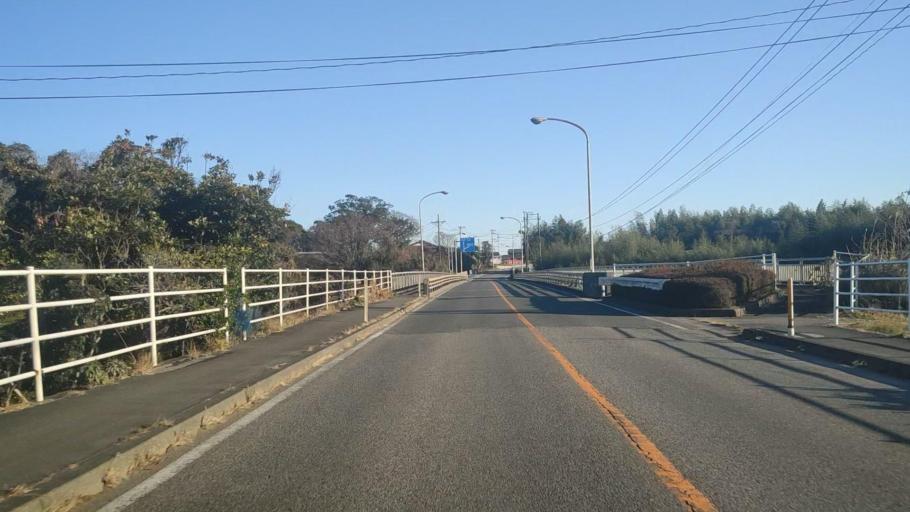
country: JP
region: Miyazaki
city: Takanabe
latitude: 32.2403
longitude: 131.5486
